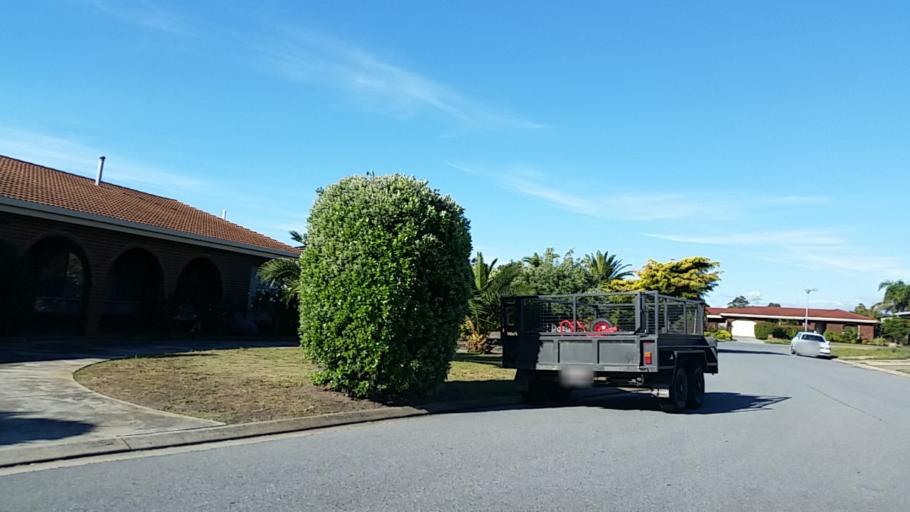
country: AU
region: South Australia
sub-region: Charles Sturt
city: Royal Park
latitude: -34.8746
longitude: 138.4998
